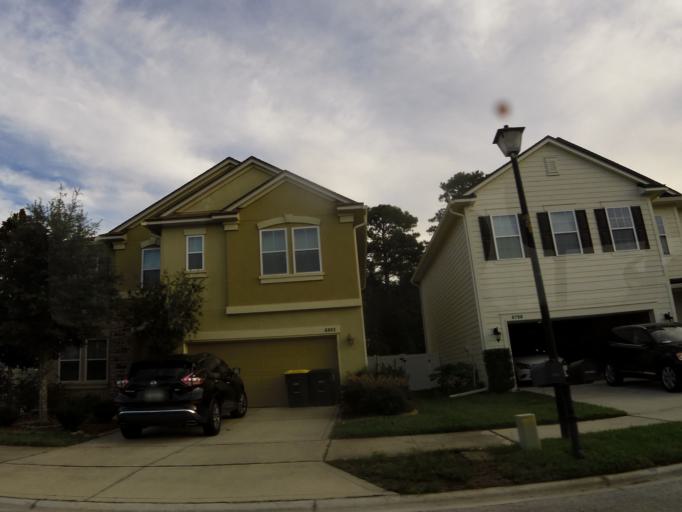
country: US
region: Florida
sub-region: Saint Johns County
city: Fruit Cove
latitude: 30.1521
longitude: -81.5307
